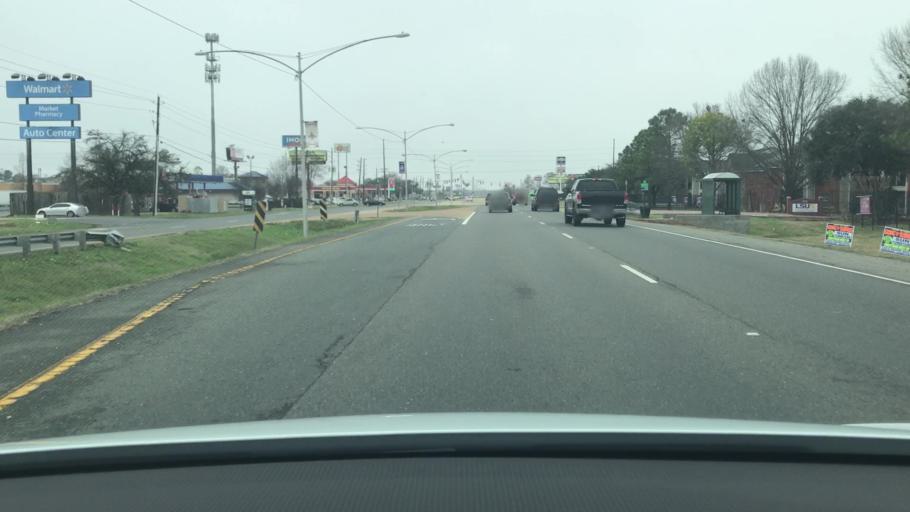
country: US
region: Louisiana
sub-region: Bossier Parish
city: Bossier City
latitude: 32.4292
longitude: -93.7102
